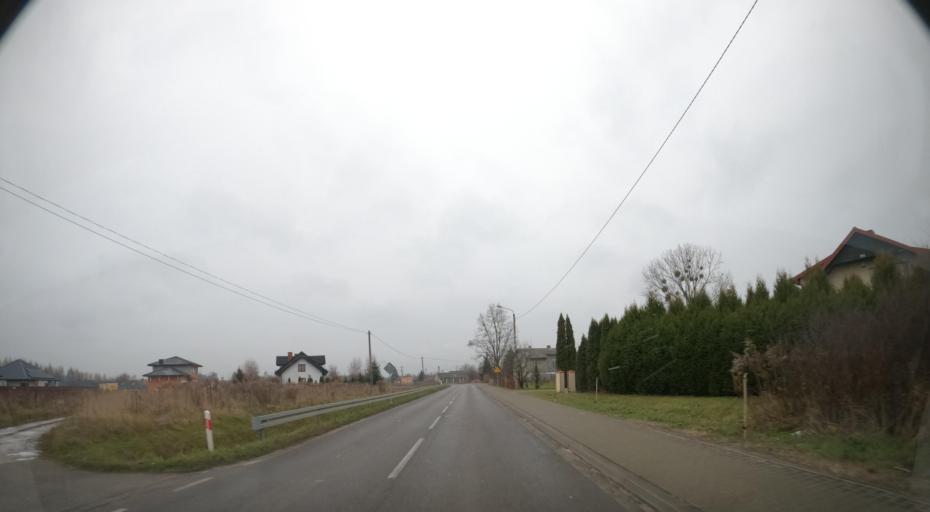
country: PL
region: Masovian Voivodeship
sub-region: Powiat radomski
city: Skaryszew
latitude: 51.3852
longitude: 21.2562
